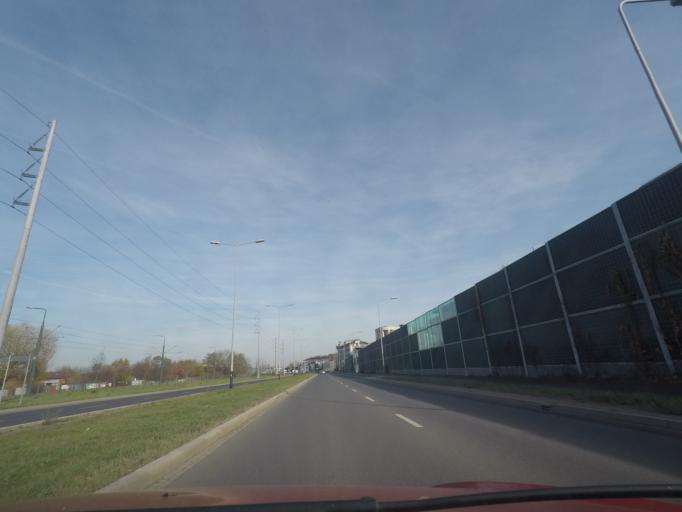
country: PL
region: Lesser Poland Voivodeship
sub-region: Krakow
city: Sidzina
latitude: 50.0215
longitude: 19.8993
